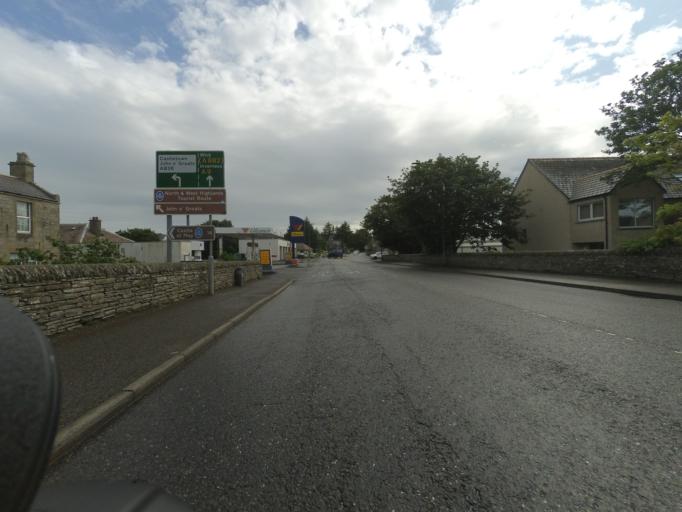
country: GB
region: Scotland
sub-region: Highland
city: Thurso
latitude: 58.5922
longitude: -3.5186
